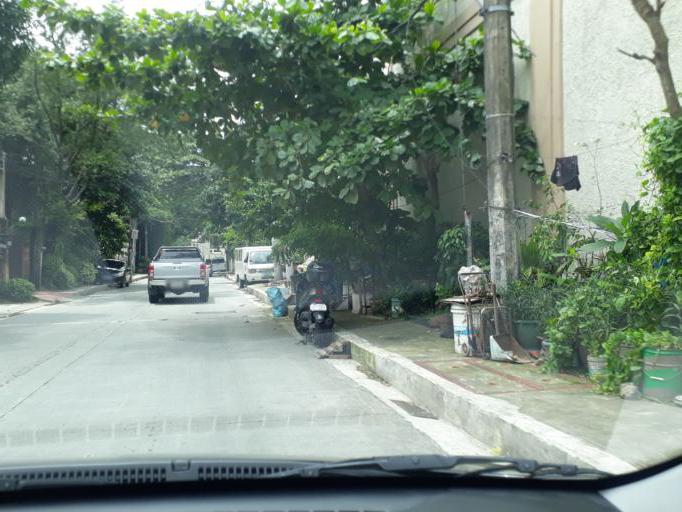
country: PH
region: Metro Manila
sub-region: San Juan
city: San Juan
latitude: 14.6197
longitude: 121.0398
